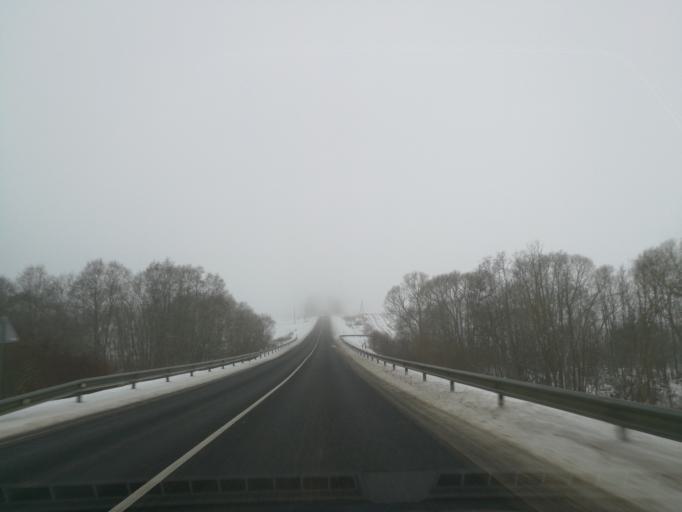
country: LT
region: Utenos apskritis
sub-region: Anyksciai
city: Anyksciai
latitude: 55.5156
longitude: 25.0497
